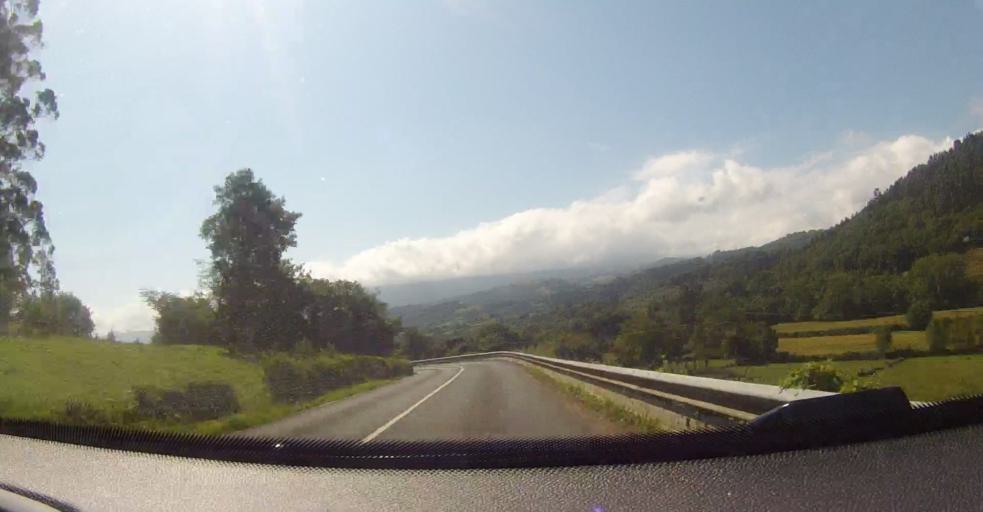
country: ES
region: Asturias
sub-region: Province of Asturias
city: Colunga
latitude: 43.4903
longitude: -5.3119
